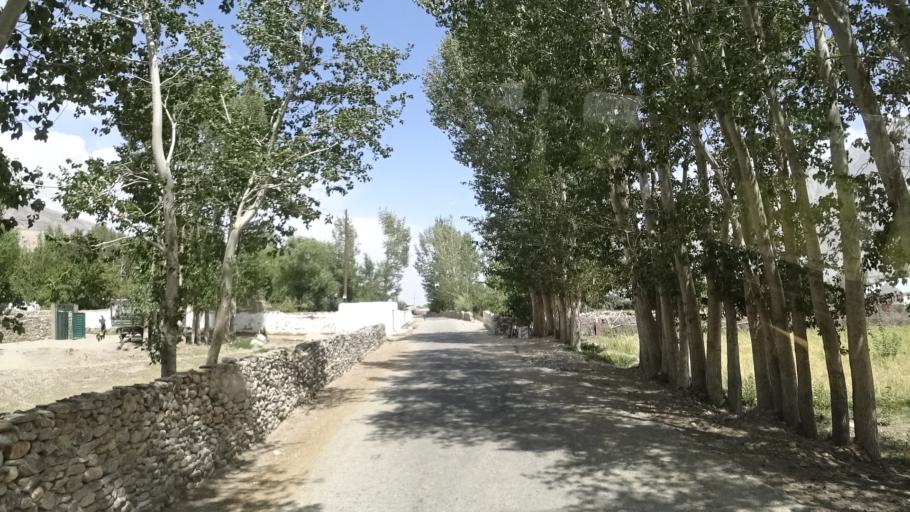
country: AF
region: Badakhshan
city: Khandud
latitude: 36.9198
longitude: 72.1897
